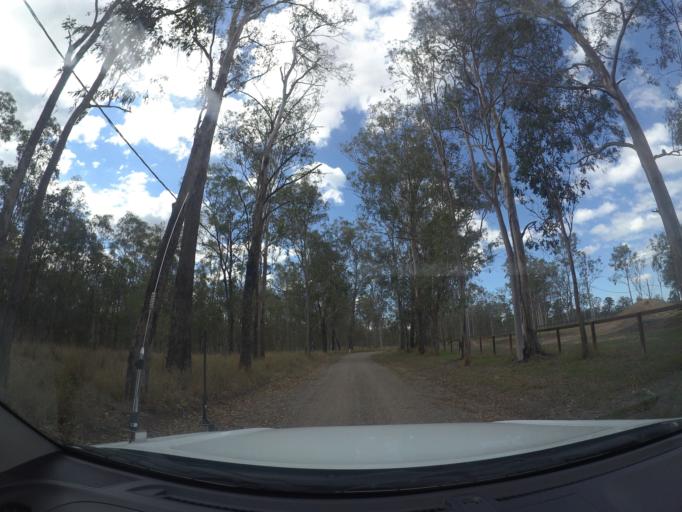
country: AU
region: Queensland
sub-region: Logan
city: North Maclean
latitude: -27.8079
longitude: 152.9935
